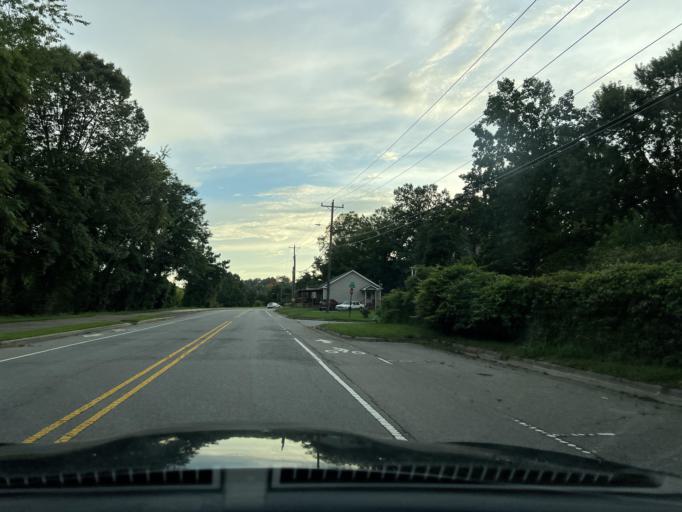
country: US
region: North Carolina
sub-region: Buncombe County
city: Asheville
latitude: 35.5806
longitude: -82.5582
